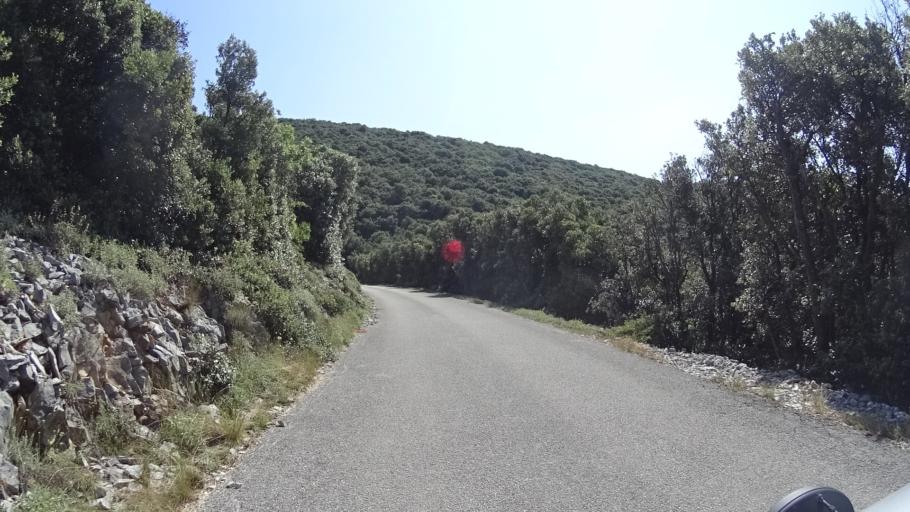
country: HR
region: Istarska
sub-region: Grad Labin
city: Rabac
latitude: 44.9750
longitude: 14.1378
